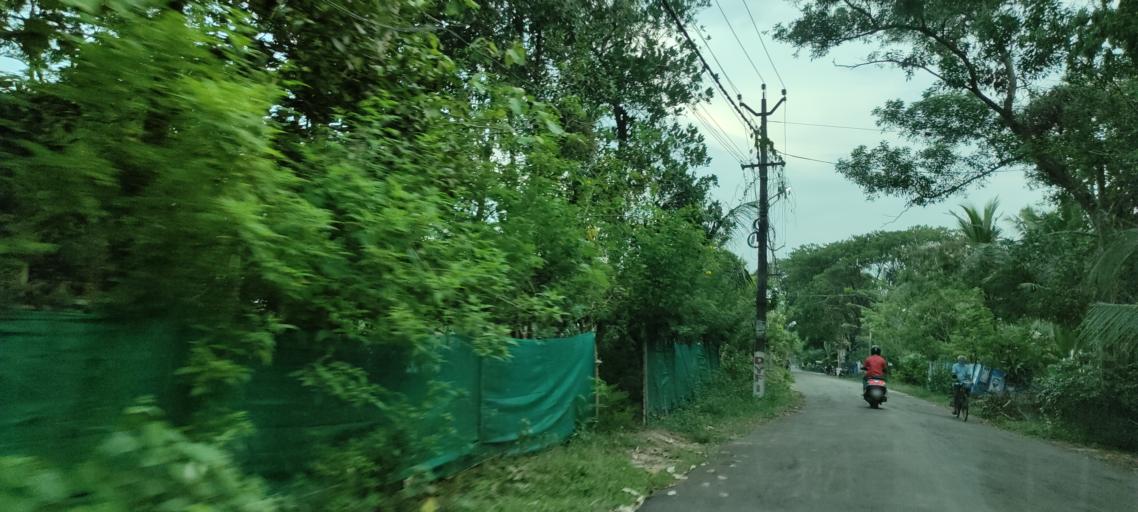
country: IN
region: Kerala
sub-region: Alappuzha
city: Shertallai
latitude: 9.6939
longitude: 76.3556
